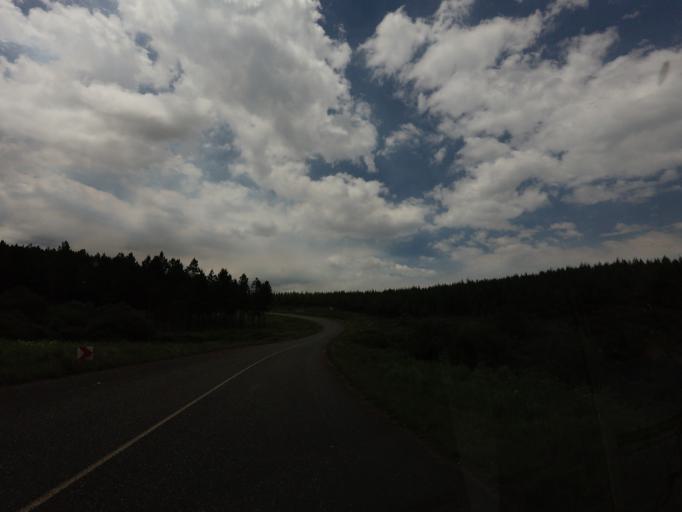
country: ZA
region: Mpumalanga
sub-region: Ehlanzeni District
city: Graksop
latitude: -24.9652
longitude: 30.8122
